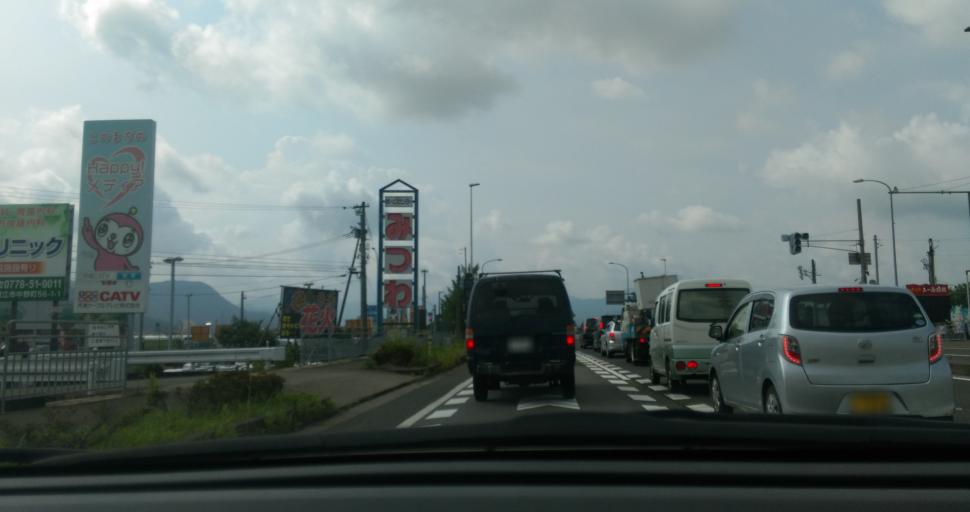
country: JP
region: Fukui
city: Sabae
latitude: 35.9566
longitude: 136.1887
